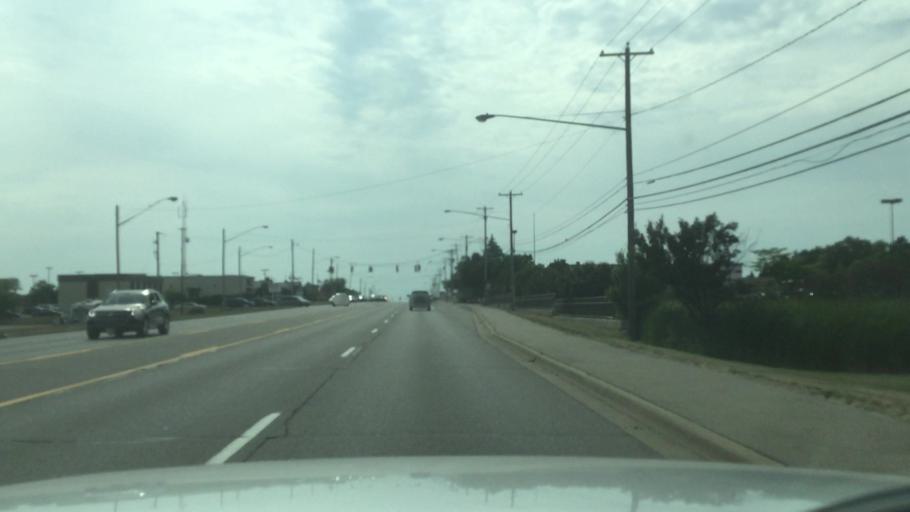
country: US
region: Michigan
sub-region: Genesee County
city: Swartz Creek
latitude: 43.0021
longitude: -83.7661
